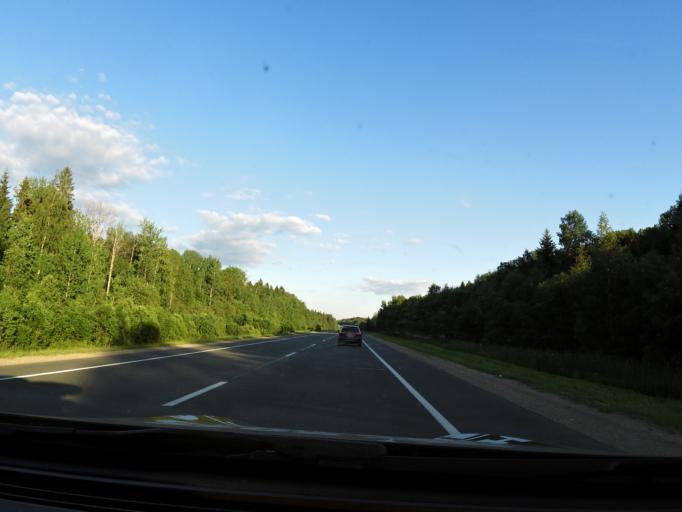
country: RU
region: Vologda
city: Vologda
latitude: 59.0889
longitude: 40.0046
